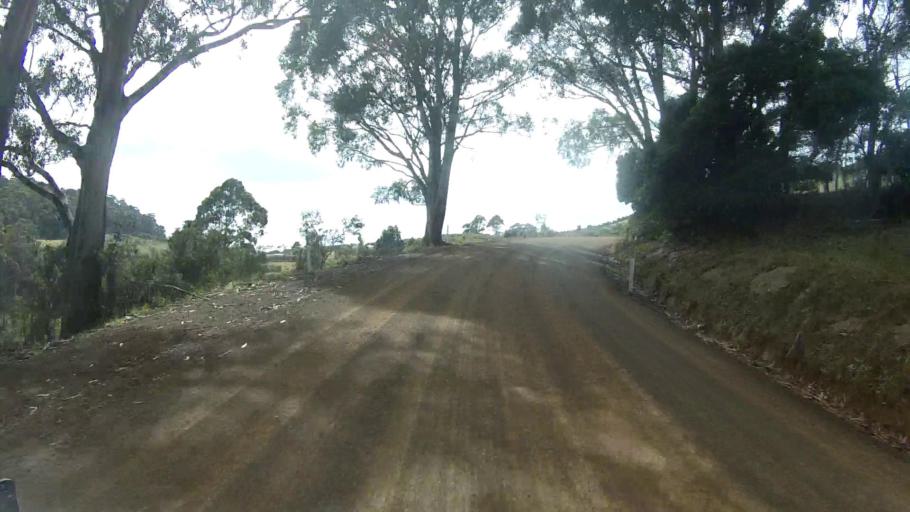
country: AU
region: Tasmania
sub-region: Sorell
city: Sorell
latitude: -42.7763
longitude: 147.8224
